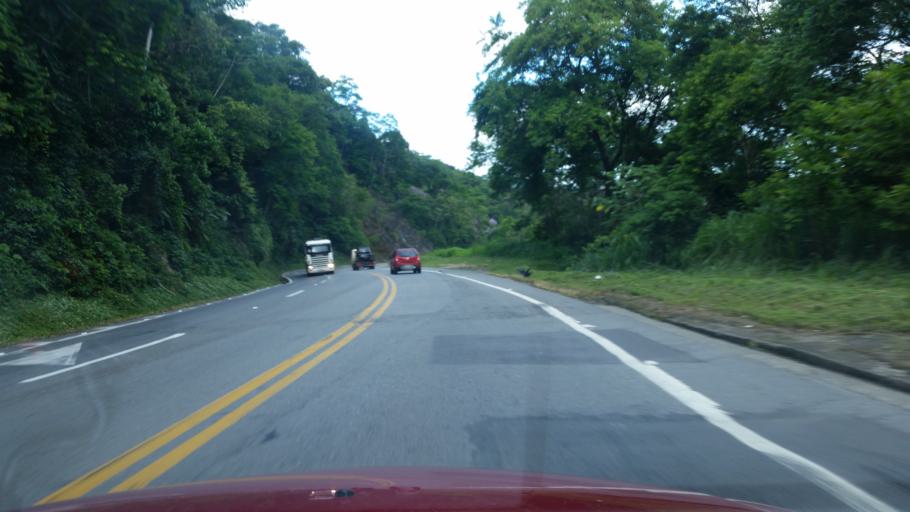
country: BR
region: Sao Paulo
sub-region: Miracatu
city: Miracatu
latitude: -24.2669
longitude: -47.2818
